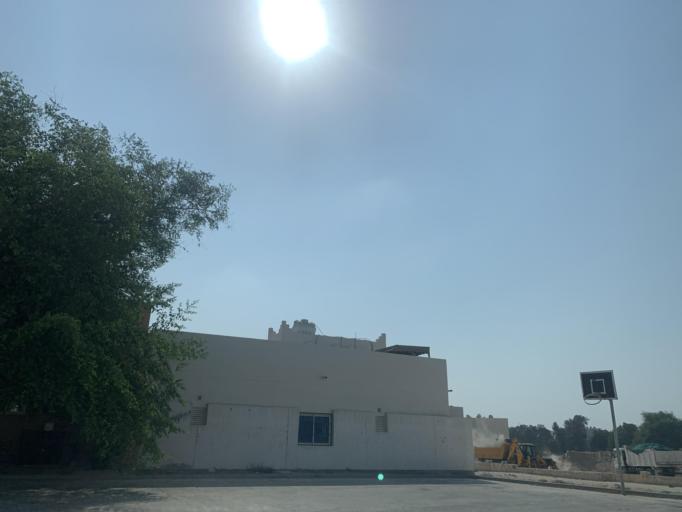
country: BH
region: Central Governorate
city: Madinat Hamad
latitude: 26.1298
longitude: 50.4928
